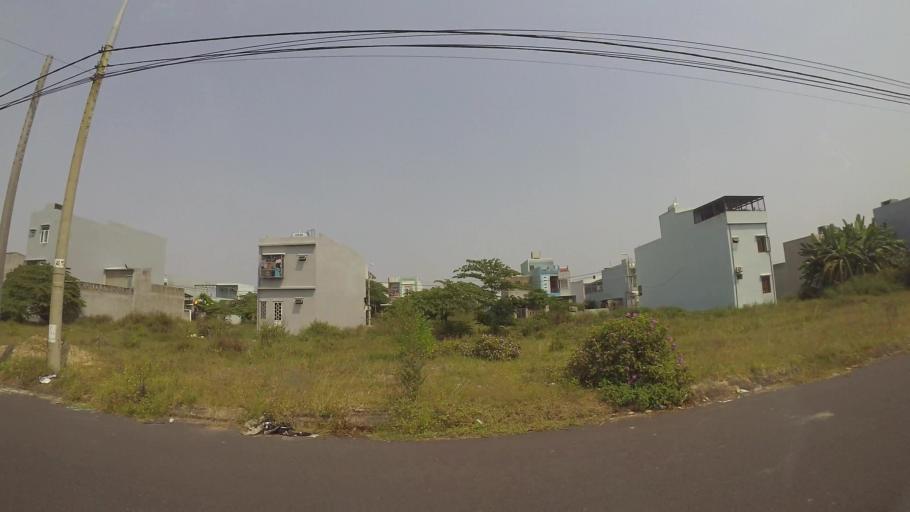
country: VN
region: Da Nang
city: Cam Le
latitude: 15.9833
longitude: 108.2111
